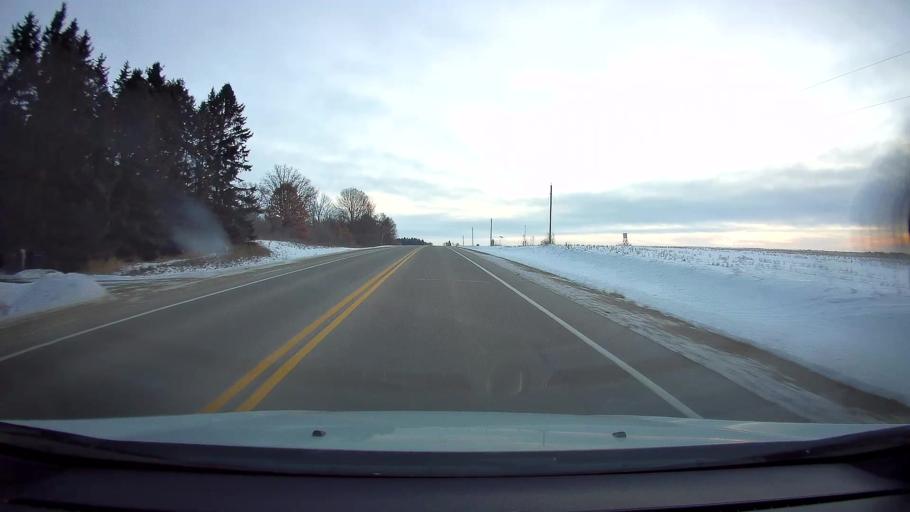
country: US
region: Wisconsin
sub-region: Saint Croix County
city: New Richmond
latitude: 45.1371
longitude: -92.4931
